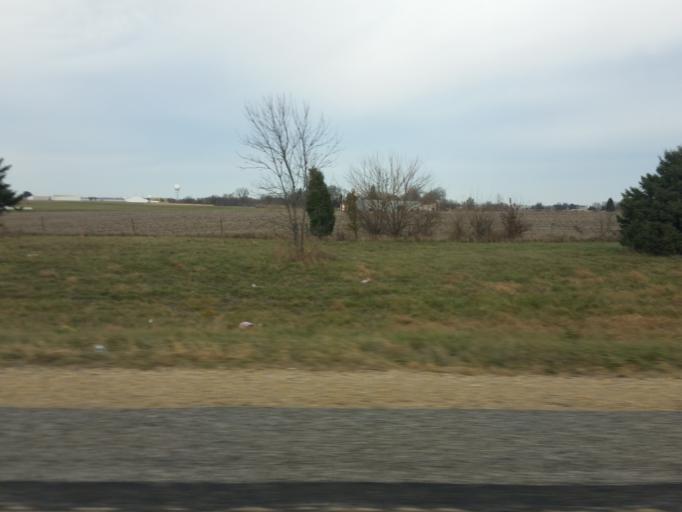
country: US
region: Iowa
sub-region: Scott County
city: Eldridge
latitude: 41.5981
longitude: -90.5808
